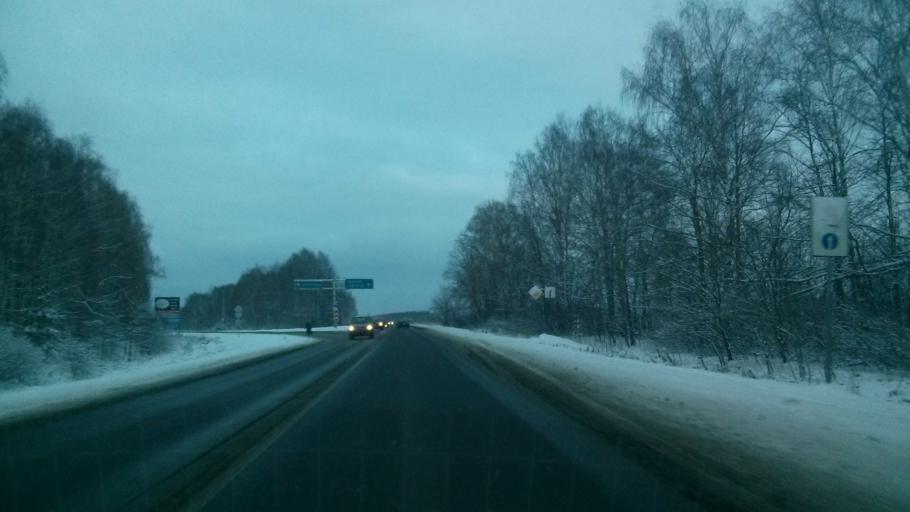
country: RU
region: Nizjnij Novgorod
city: Bogorodsk
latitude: 56.0804
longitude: 43.4737
